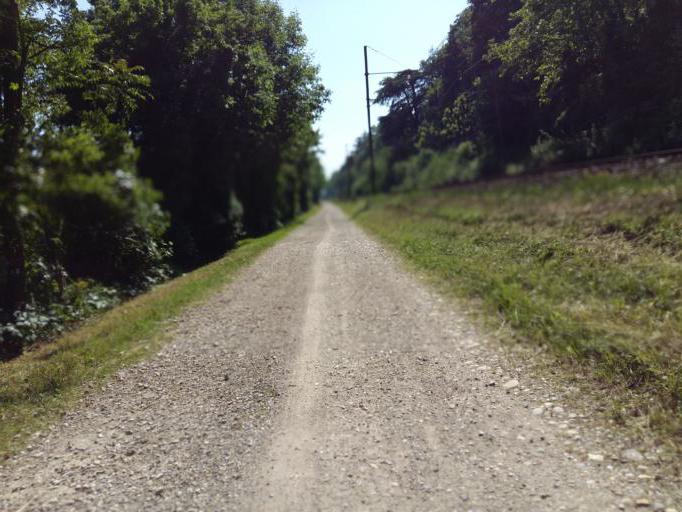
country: FR
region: Rhone-Alpes
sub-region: Departement du Rhone
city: Rillieux-la-Pape
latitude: 45.7999
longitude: 4.8833
